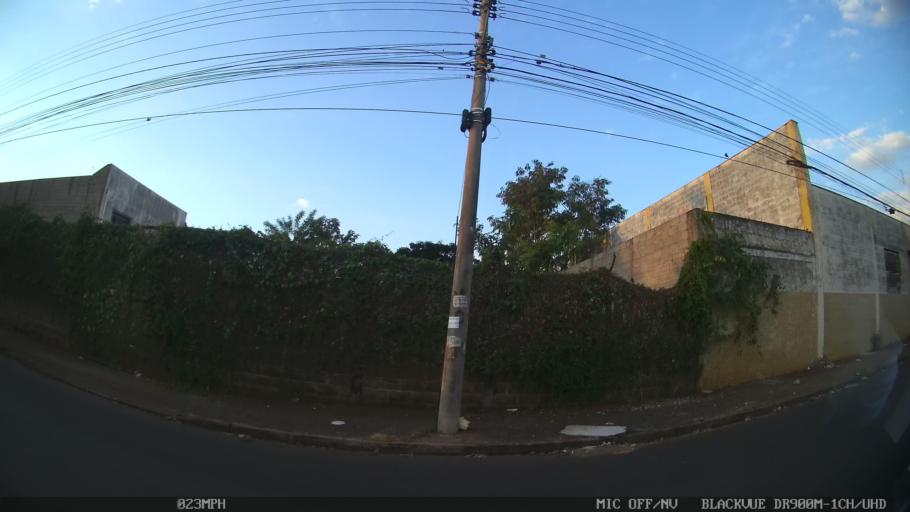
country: BR
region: Sao Paulo
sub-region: Ribeirao Preto
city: Ribeirao Preto
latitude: -21.1482
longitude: -47.7890
